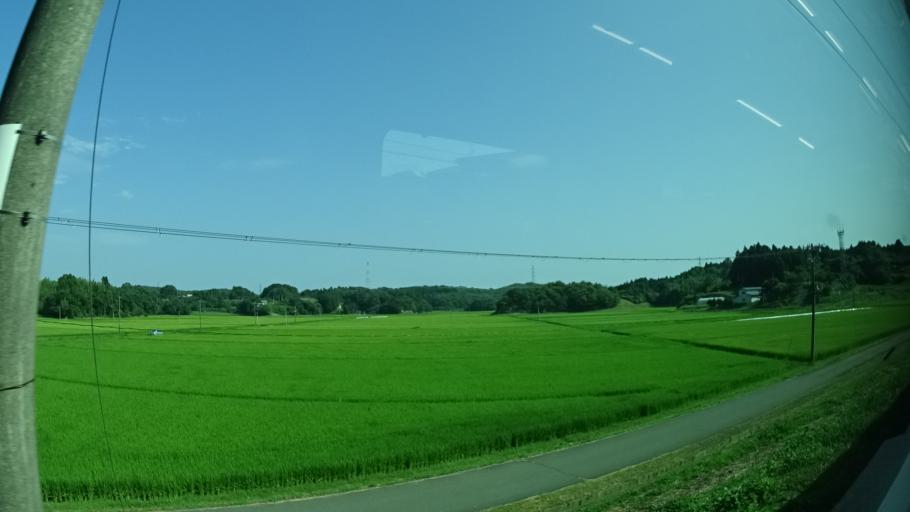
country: JP
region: Miyagi
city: Matsushima
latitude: 38.4323
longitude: 141.0833
